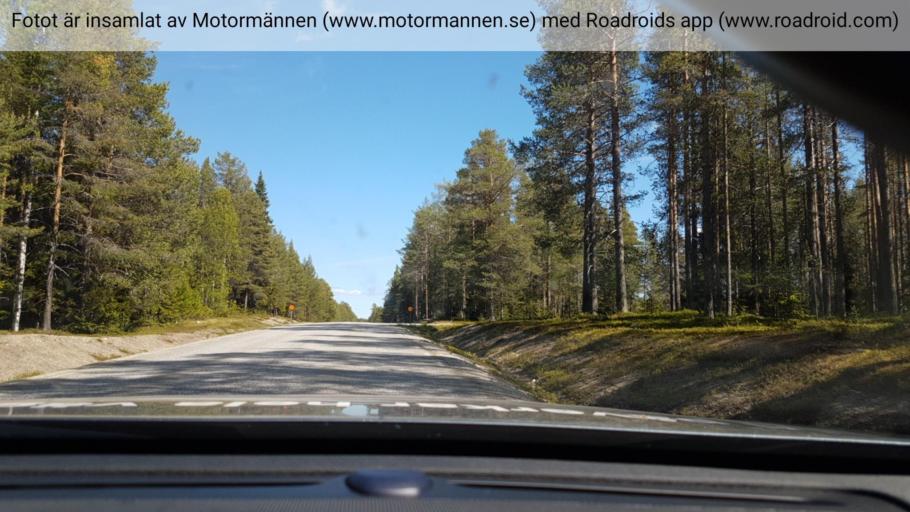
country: SE
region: Vaesterbotten
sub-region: Lycksele Kommun
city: Soderfors
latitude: 64.6254
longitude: 18.0787
